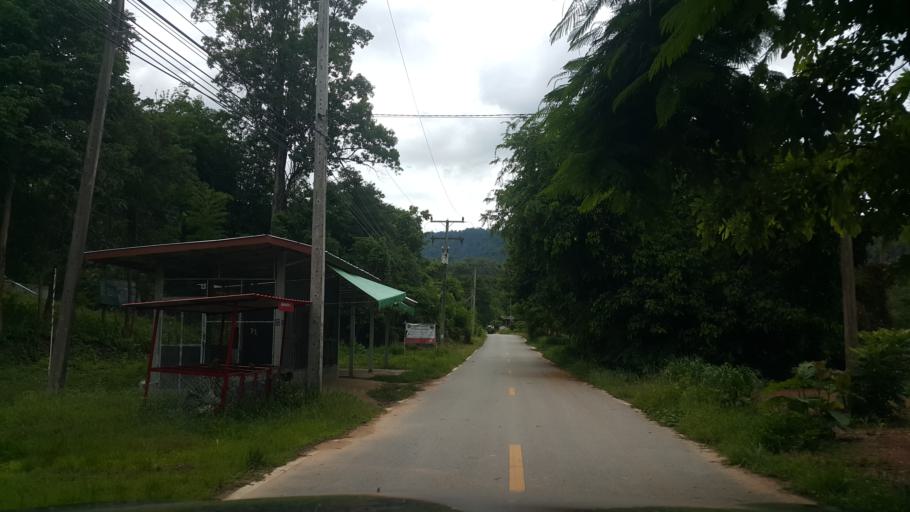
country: TH
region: Phitsanulok
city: Chat Trakan
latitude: 17.3020
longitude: 100.6725
